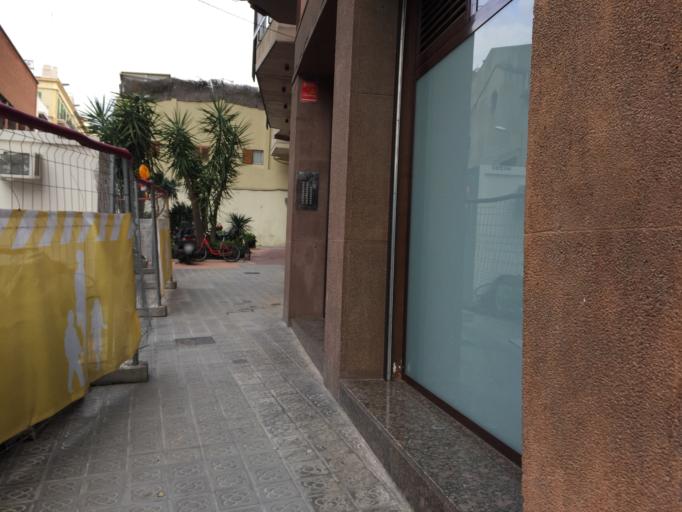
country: ES
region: Catalonia
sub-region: Provincia de Barcelona
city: Gracia
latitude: 41.4074
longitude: 2.1516
